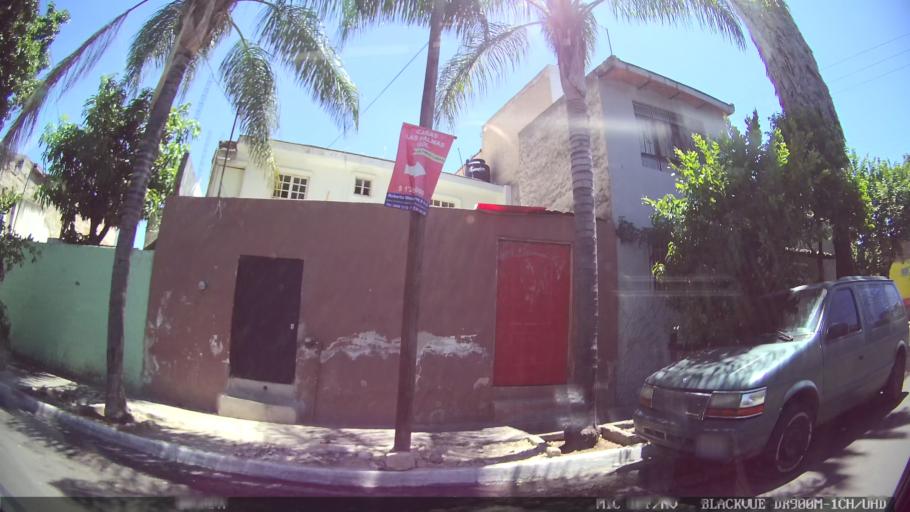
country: MX
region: Jalisco
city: Tlaquepaque
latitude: 20.6713
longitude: -103.2715
